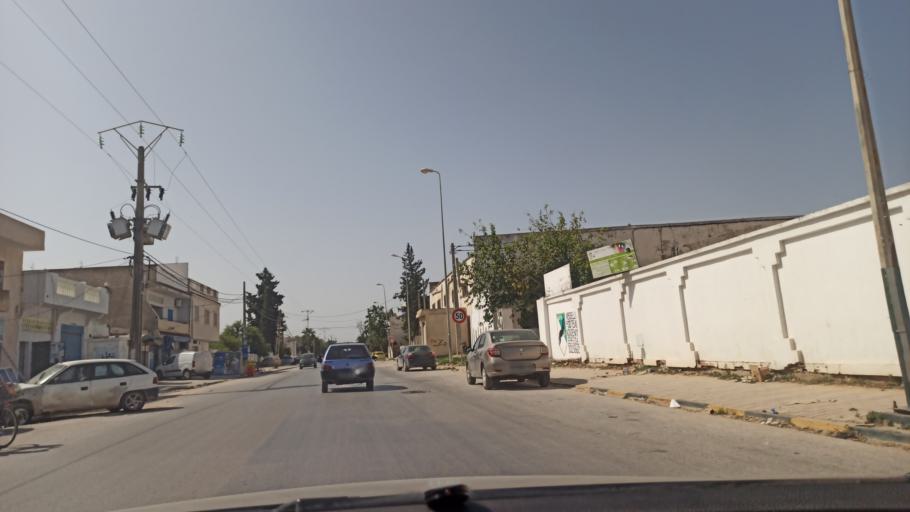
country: TN
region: Manouba
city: Manouba
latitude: 36.7611
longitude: 10.1076
